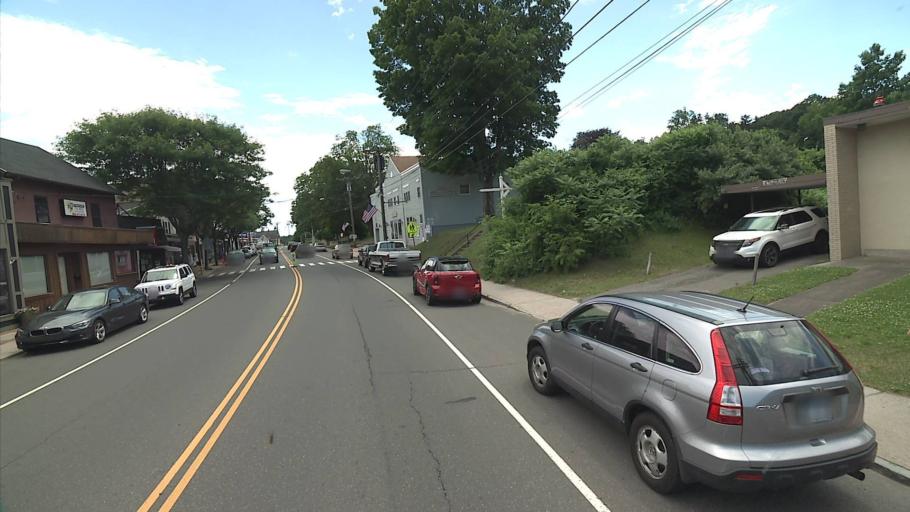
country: US
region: Connecticut
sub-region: Litchfield County
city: Watertown
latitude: 41.6016
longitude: -73.1159
